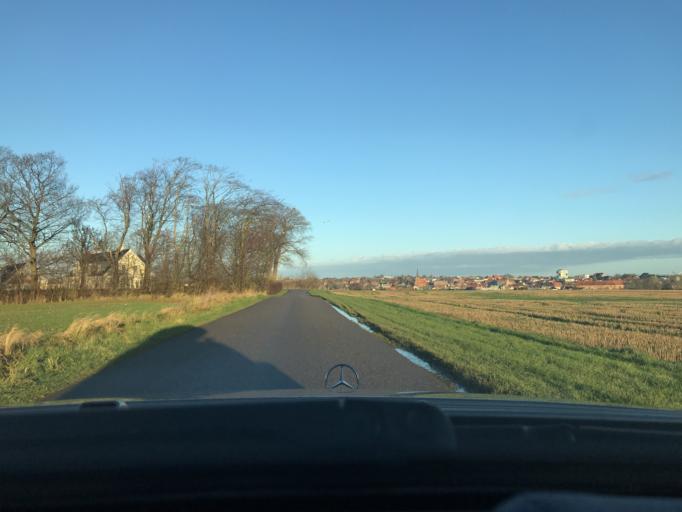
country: DK
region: South Denmark
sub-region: Sonderborg Kommune
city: Dybbol
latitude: 54.9037
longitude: 9.7683
